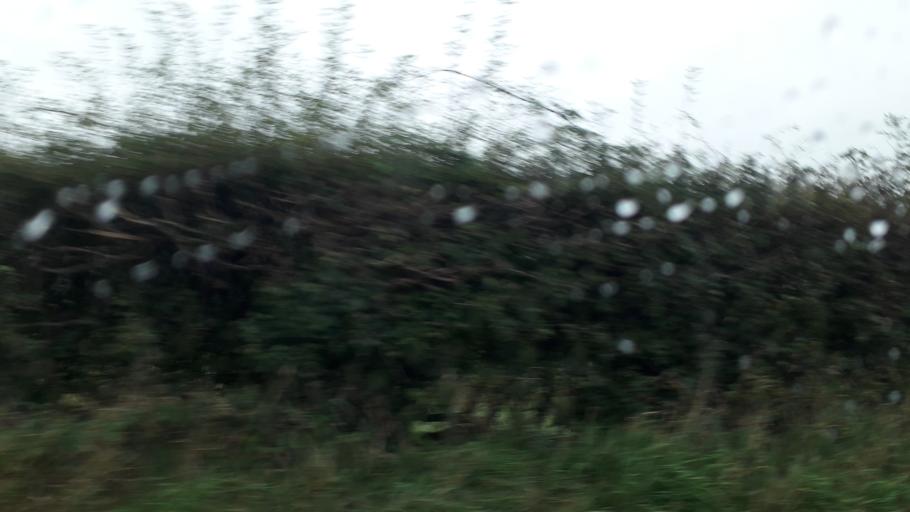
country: IE
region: Connaught
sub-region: Roscommon
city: Boyle
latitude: 53.7898
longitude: -8.2735
